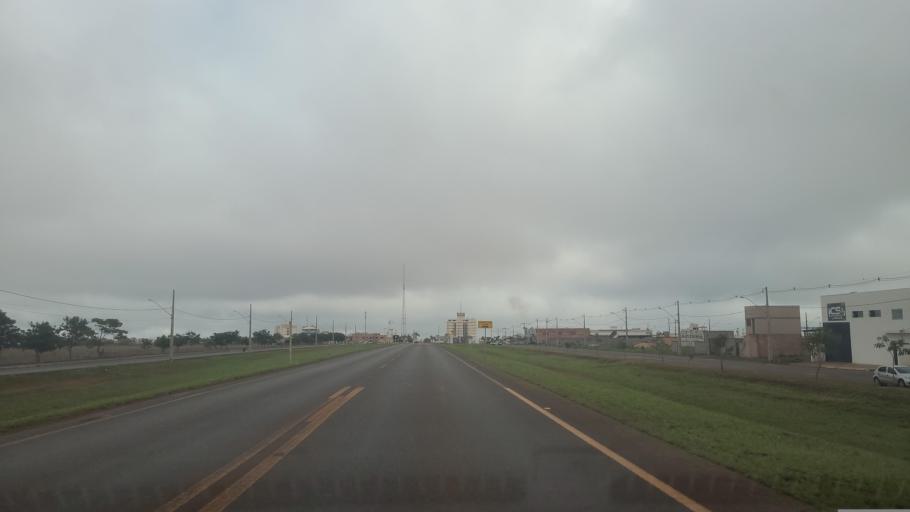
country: BR
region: Minas Gerais
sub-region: Sao Gotardo
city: Sao Gotardo
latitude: -19.2055
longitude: -46.2308
